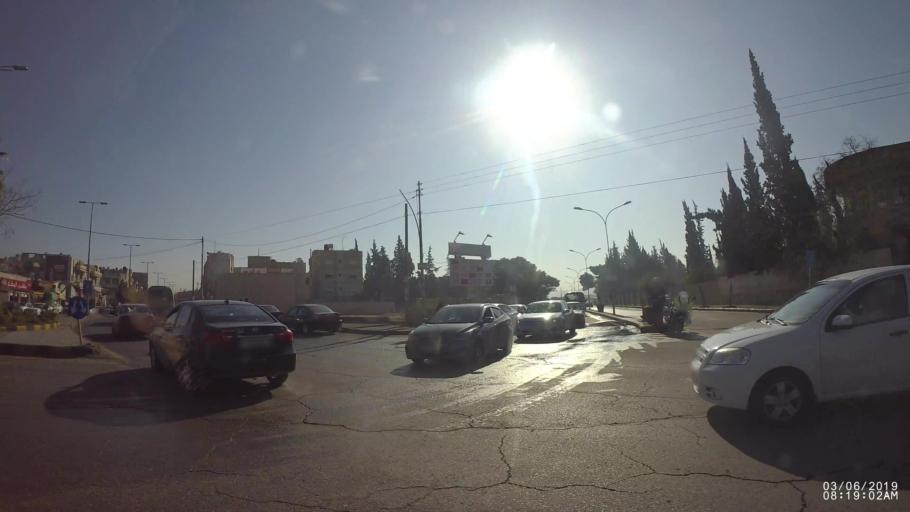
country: JO
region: Amman
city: Amman
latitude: 31.9783
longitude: 35.9799
